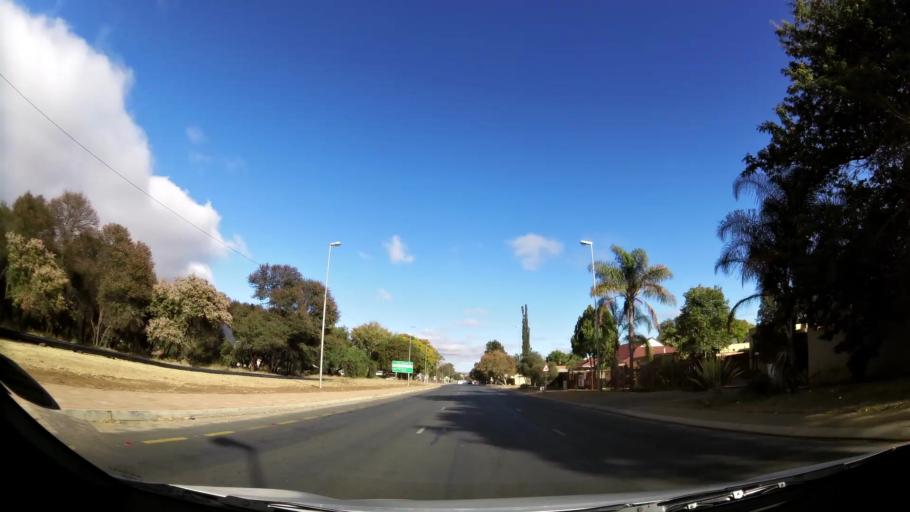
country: ZA
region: Limpopo
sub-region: Capricorn District Municipality
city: Polokwane
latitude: -23.9184
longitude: 29.4646
